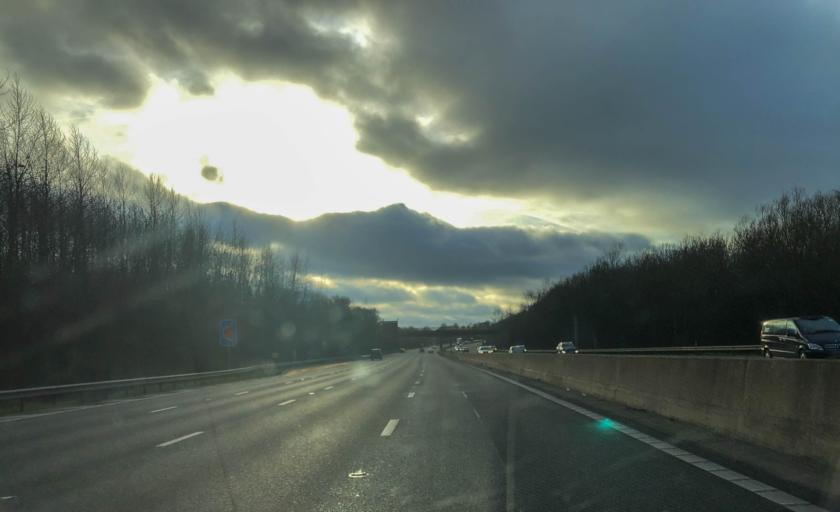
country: GB
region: England
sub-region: Surrey
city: Woldingham
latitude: 51.2650
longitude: -0.0270
